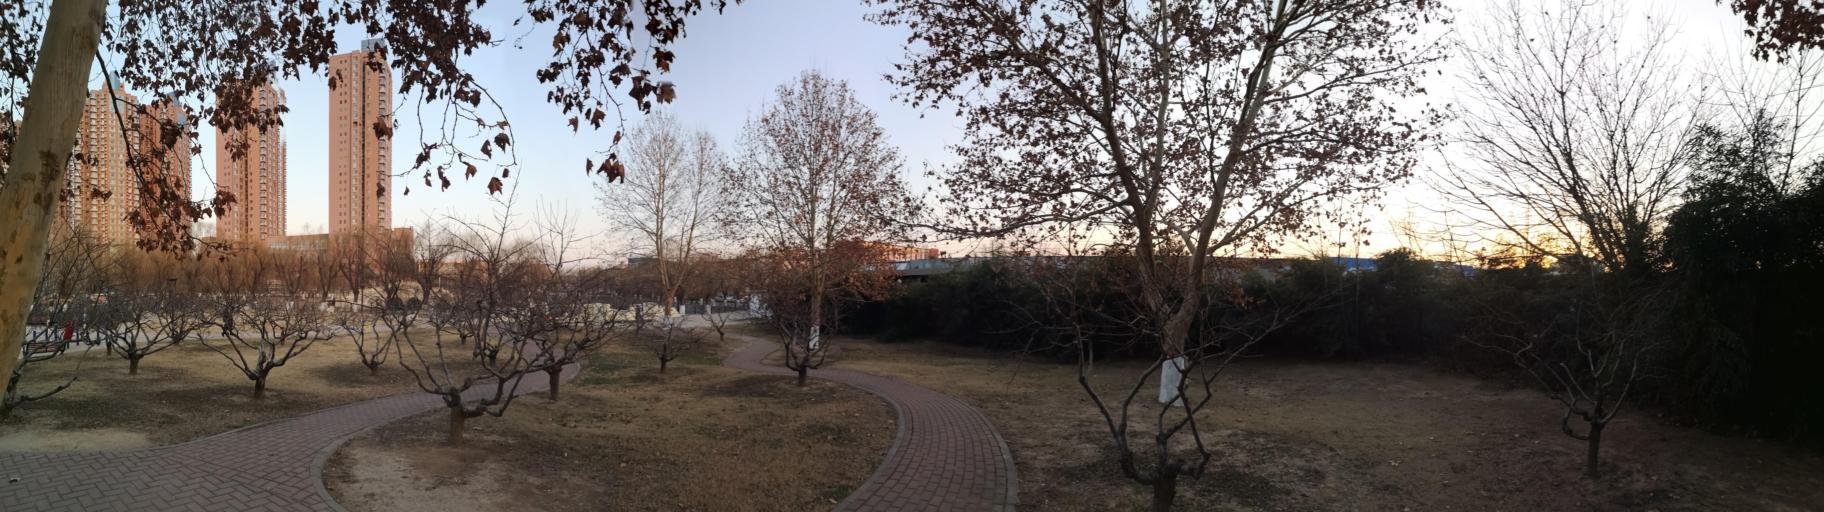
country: CN
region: Henan Sheng
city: Zhongyuanlu
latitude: 35.7724
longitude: 115.0782
